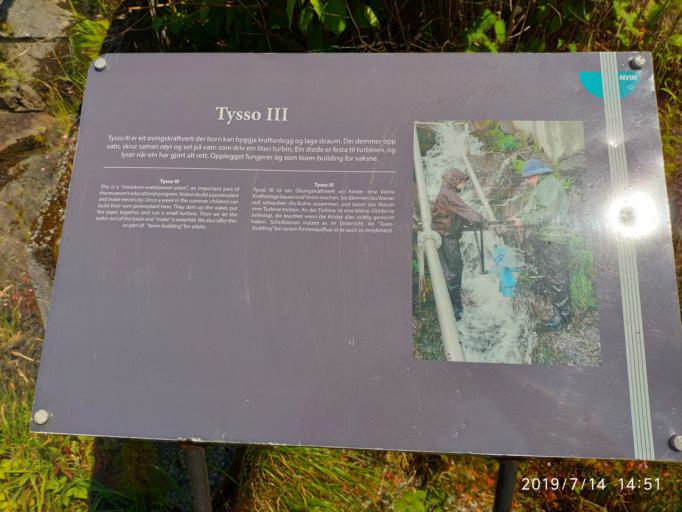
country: NO
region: Hordaland
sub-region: Odda
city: Odda
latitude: 60.1204
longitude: 6.5566
